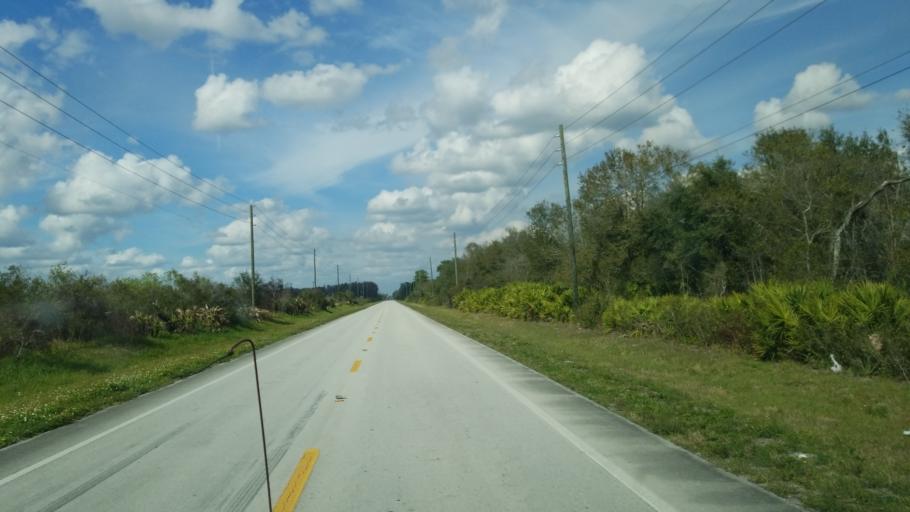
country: US
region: Florida
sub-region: Osceola County
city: Saint Cloud
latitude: 28.1017
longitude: -81.0762
